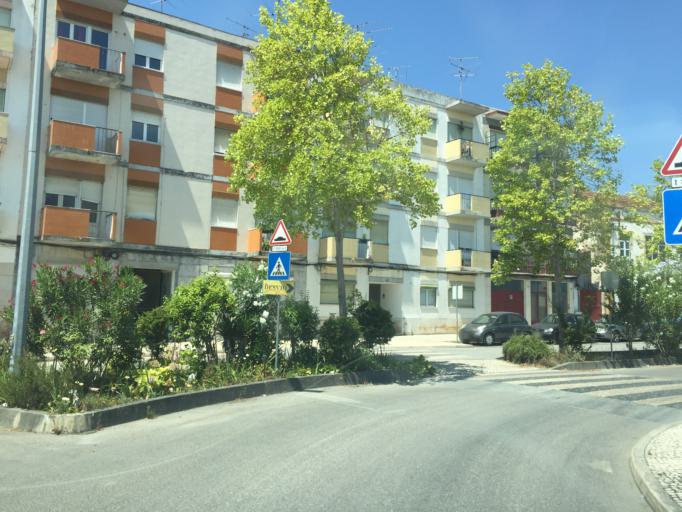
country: PT
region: Santarem
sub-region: Tomar
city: Tomar
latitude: 39.5963
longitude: -8.4122
